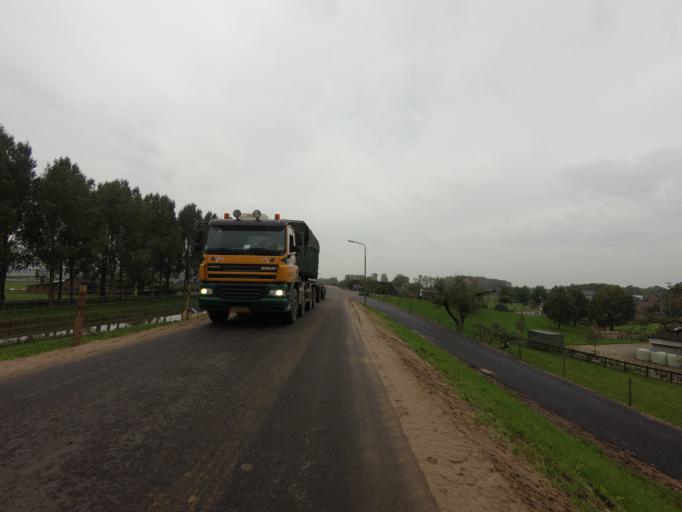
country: NL
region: South Holland
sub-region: Gemeente Leerdam
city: Leerdam
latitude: 51.9263
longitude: 5.1439
